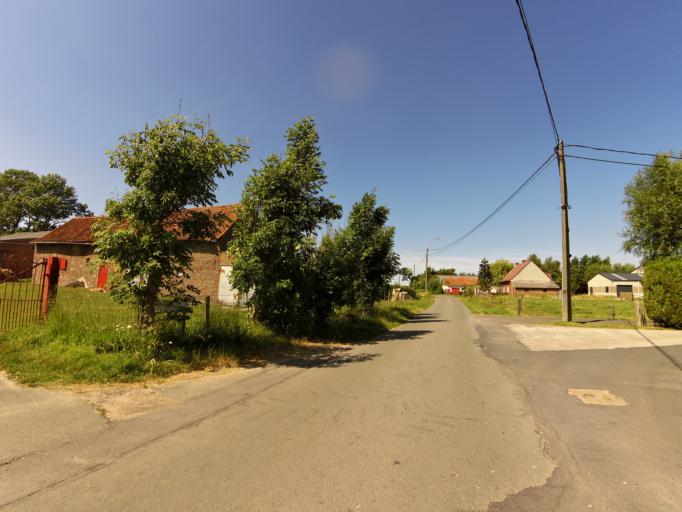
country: BE
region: Flanders
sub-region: Provincie West-Vlaanderen
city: Ichtegem
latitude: 51.1455
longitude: 3.0426
